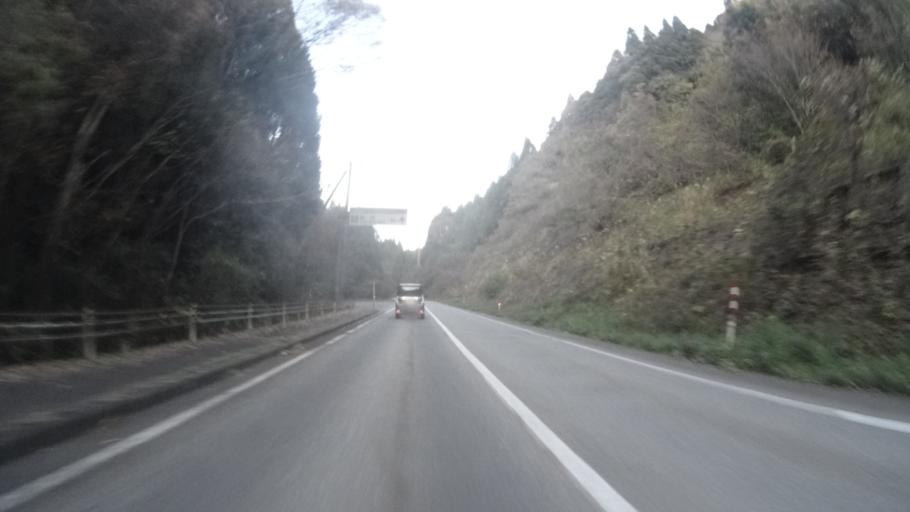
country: JP
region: Ishikawa
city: Nanao
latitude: 37.3231
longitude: 136.8172
